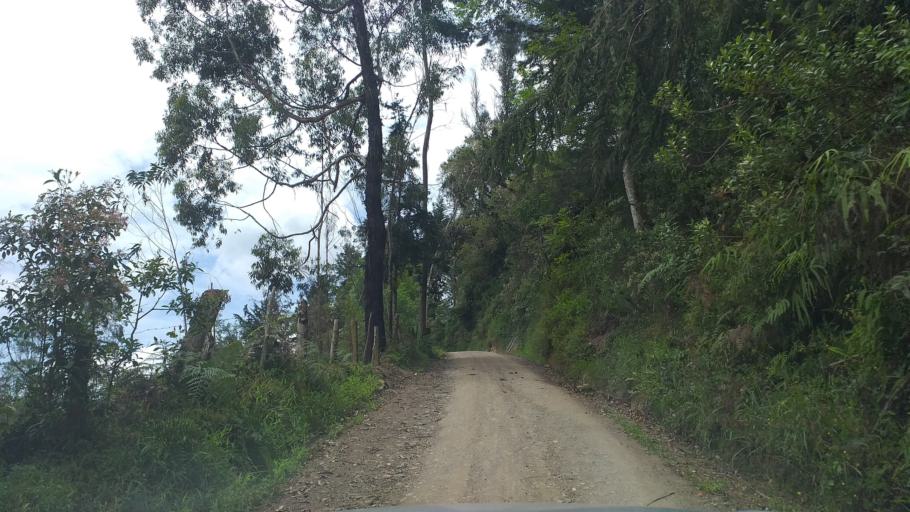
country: CO
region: Cundinamarca
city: Tenza
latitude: 5.0813
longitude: -73.4568
